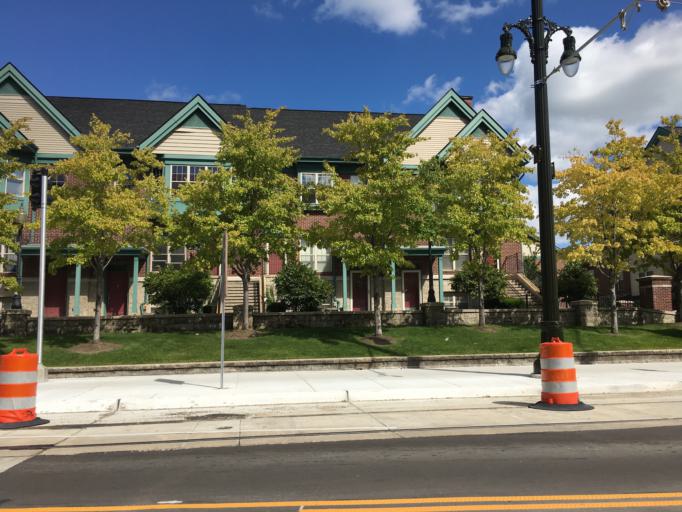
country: US
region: Michigan
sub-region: Wayne County
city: Detroit
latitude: 42.3415
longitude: -83.0538
